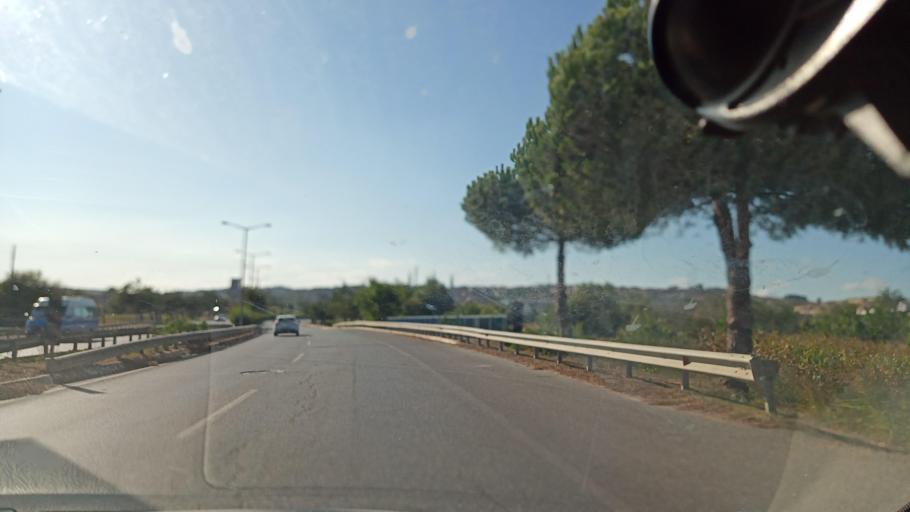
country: TR
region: Sakarya
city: Kazimpasa
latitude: 40.8491
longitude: 30.3224
